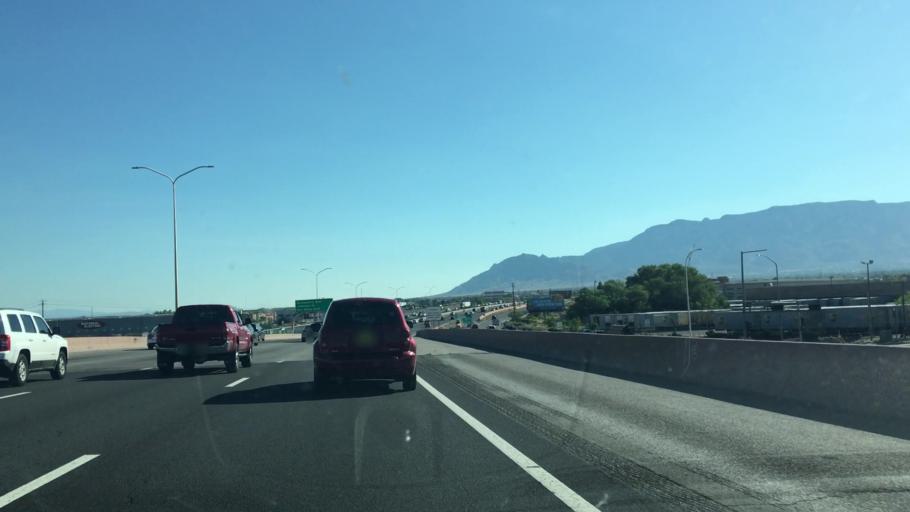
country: US
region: New Mexico
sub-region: Bernalillo County
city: Lee Acres
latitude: 35.1230
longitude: -106.6214
